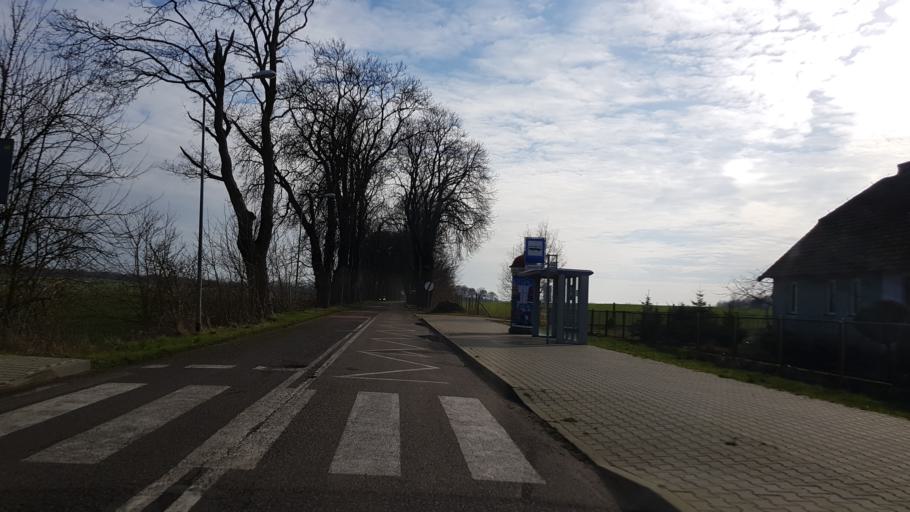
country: PL
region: West Pomeranian Voivodeship
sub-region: Powiat policki
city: Dobra
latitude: 53.5513
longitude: 14.3098
